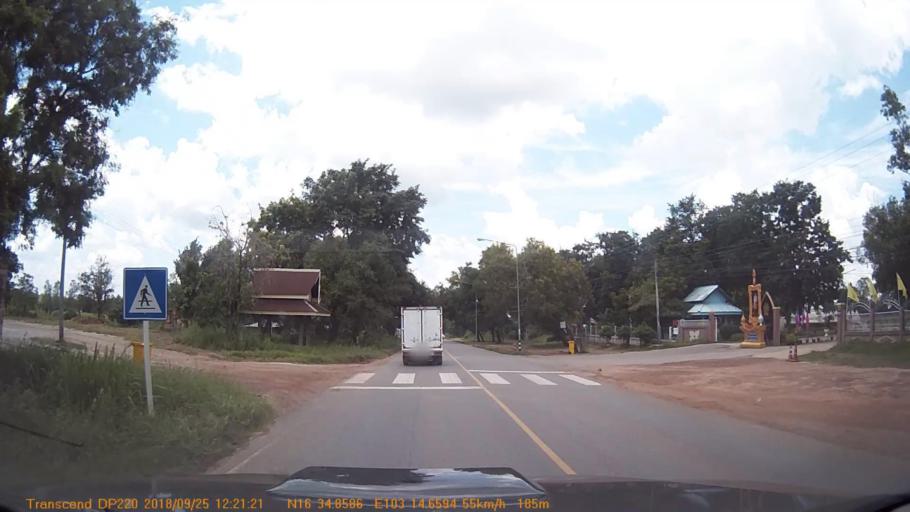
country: TH
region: Kalasin
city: Huai Mek
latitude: 16.5809
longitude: 103.2444
